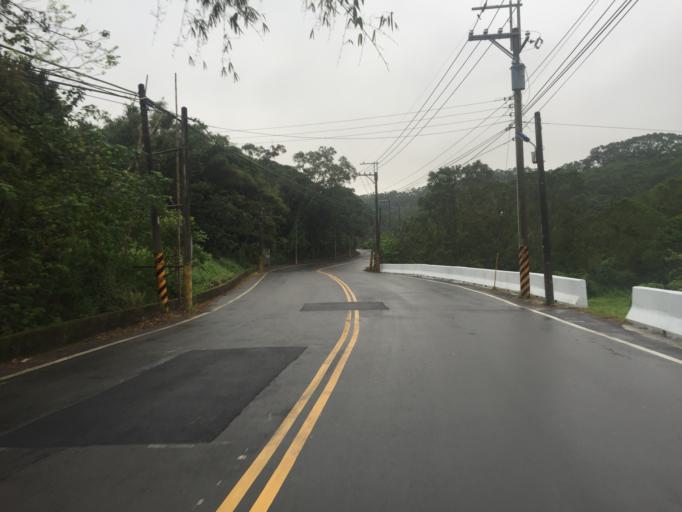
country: TW
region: Taiwan
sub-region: Hsinchu
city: Hsinchu
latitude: 24.7661
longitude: 120.9473
